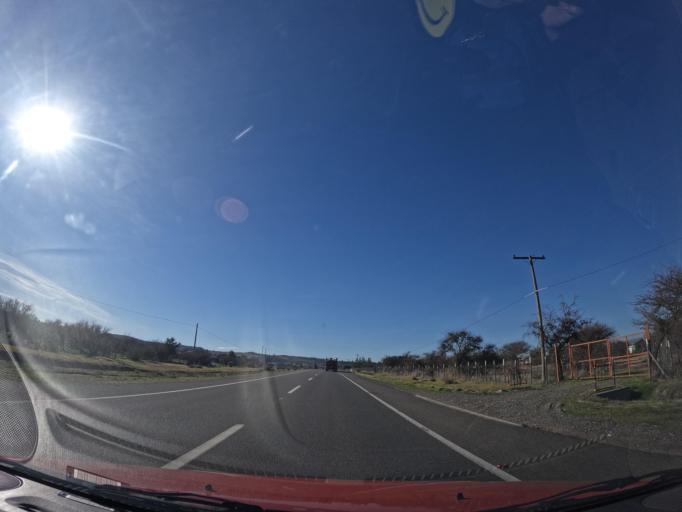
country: CL
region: Maule
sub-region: Provincia de Cauquenes
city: Cauquenes
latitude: -35.9527
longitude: -72.2087
